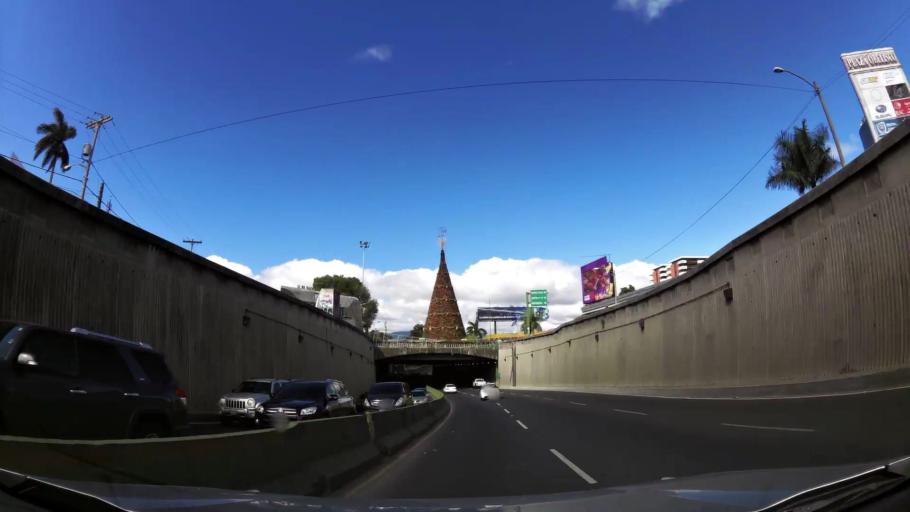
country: GT
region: Guatemala
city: Santa Catarina Pinula
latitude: 14.5944
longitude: -90.5165
